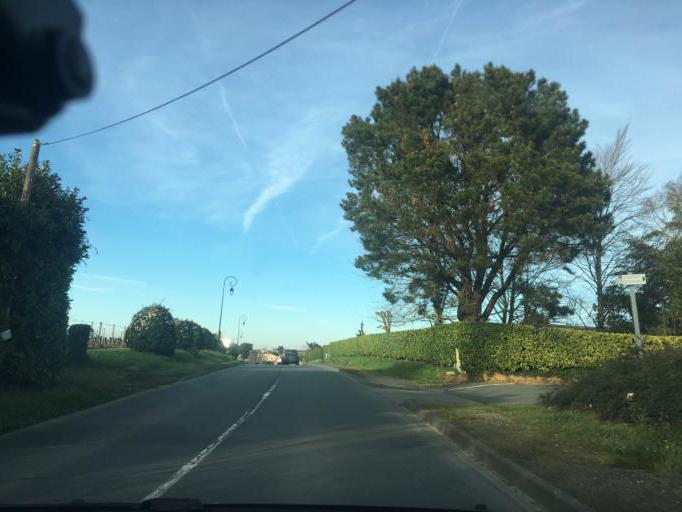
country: FR
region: Aquitaine
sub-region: Departement de la Gironde
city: Saint-Germain-du-Puch
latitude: 44.8513
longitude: -0.3262
